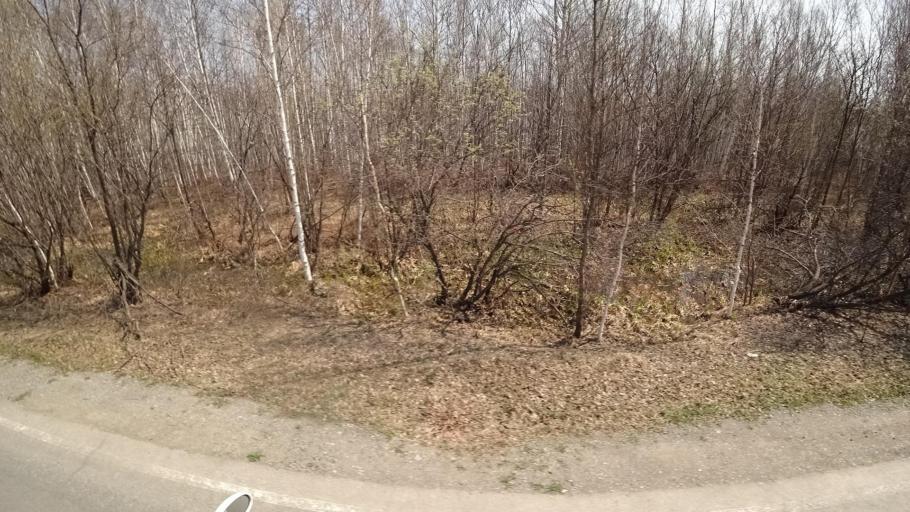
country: RU
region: Khabarovsk Krai
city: Selikhino
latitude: 50.3936
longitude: 137.3740
